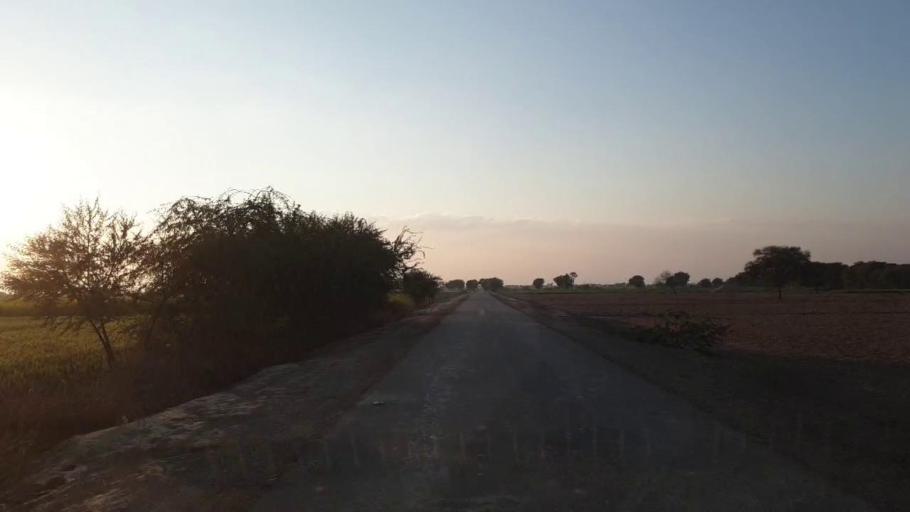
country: PK
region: Sindh
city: Shahpur Chakar
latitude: 26.1556
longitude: 68.5585
